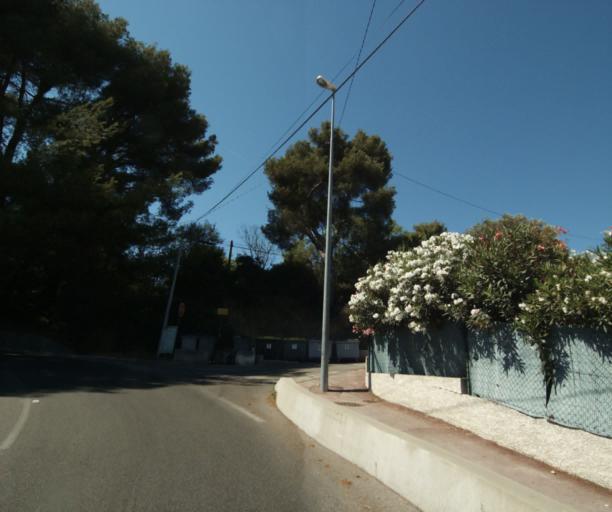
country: FR
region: Provence-Alpes-Cote d'Azur
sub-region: Departement du Var
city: La Garde
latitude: 43.1333
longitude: 6.0098
